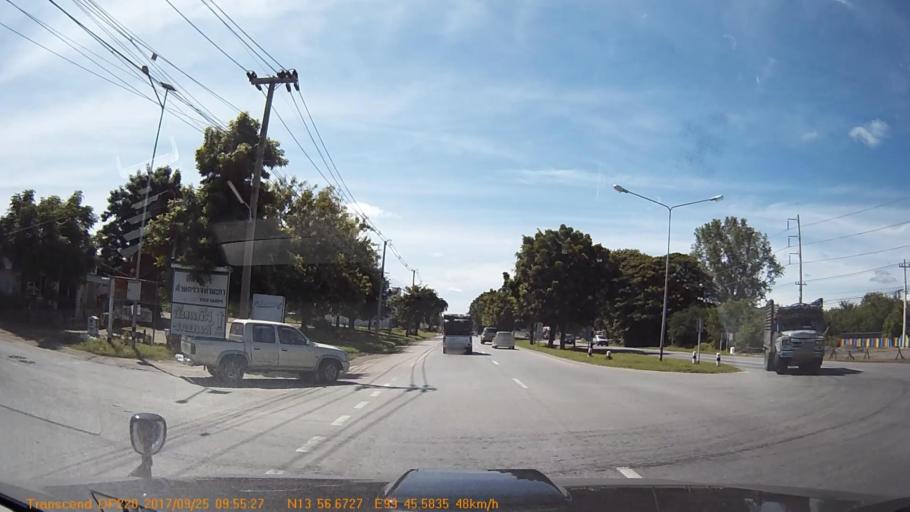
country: TH
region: Kanchanaburi
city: Tha Maka
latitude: 13.9441
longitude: 99.7599
